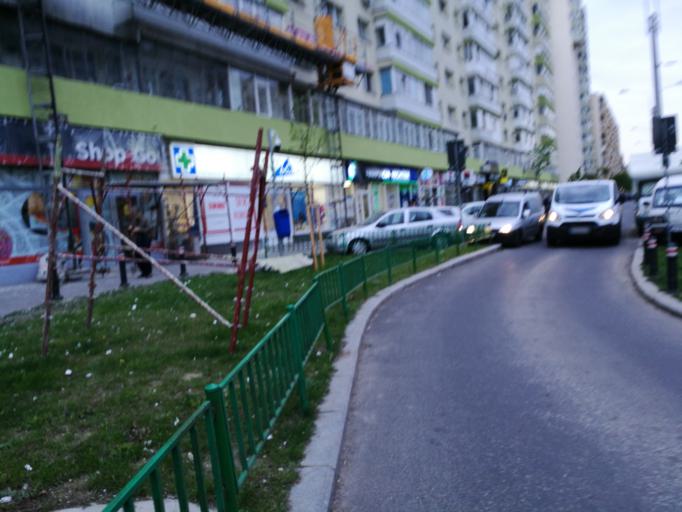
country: RO
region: Ilfov
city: Dobroesti
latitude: 44.4420
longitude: 26.1719
